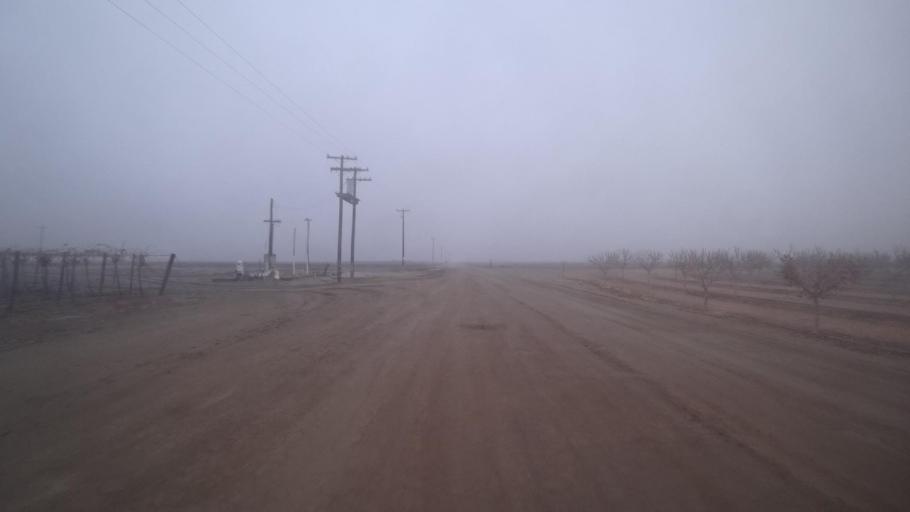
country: US
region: California
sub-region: Kern County
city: Buttonwillow
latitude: 35.4662
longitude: -119.5649
